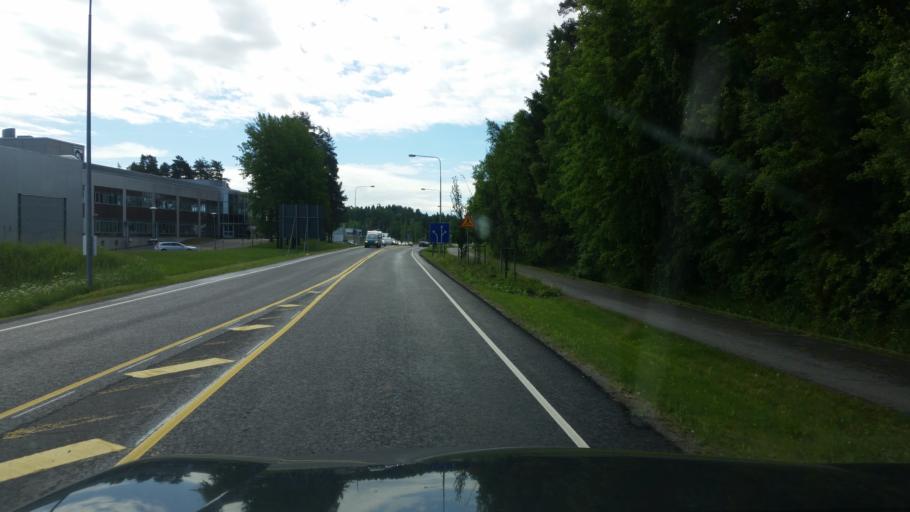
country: FI
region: Varsinais-Suomi
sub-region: Turku
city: Kaarina
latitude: 60.4186
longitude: 22.3820
